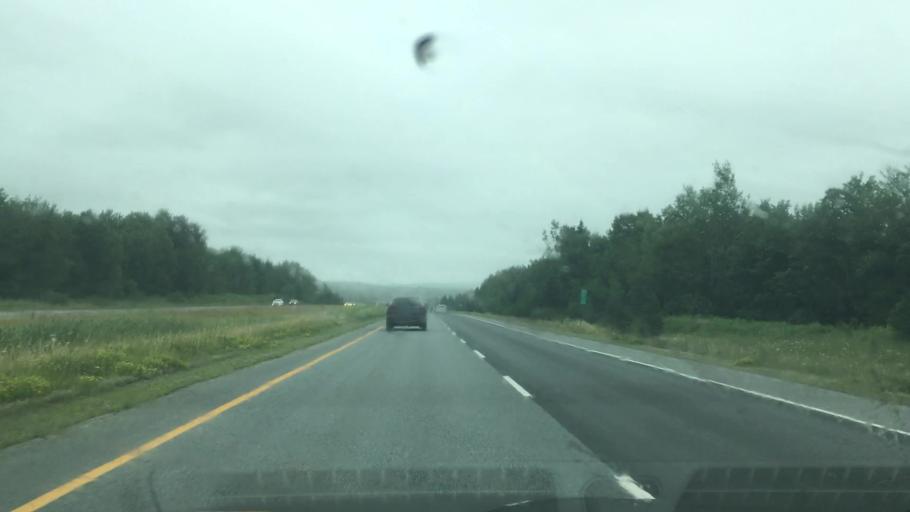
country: CA
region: Nova Scotia
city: Truro
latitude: 45.2395
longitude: -63.2935
